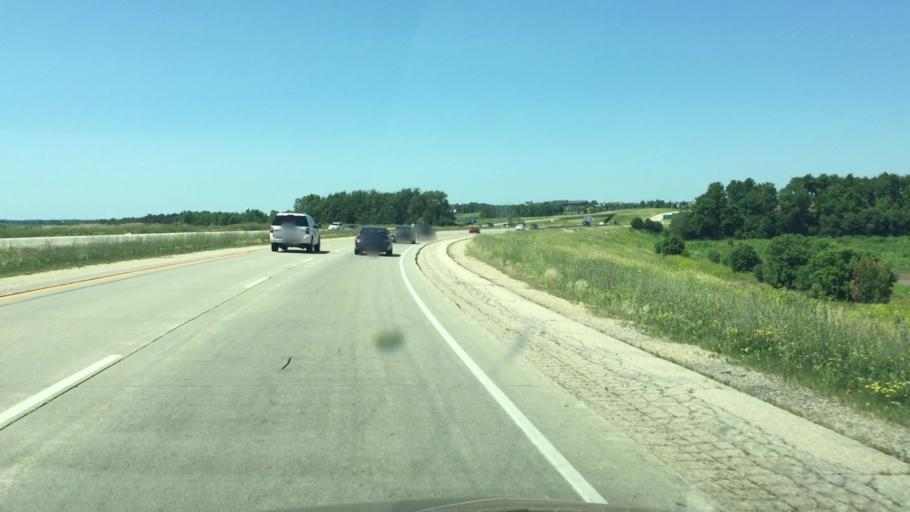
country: US
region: Wisconsin
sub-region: Dane County
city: Verona
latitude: 42.9777
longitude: -89.5557
